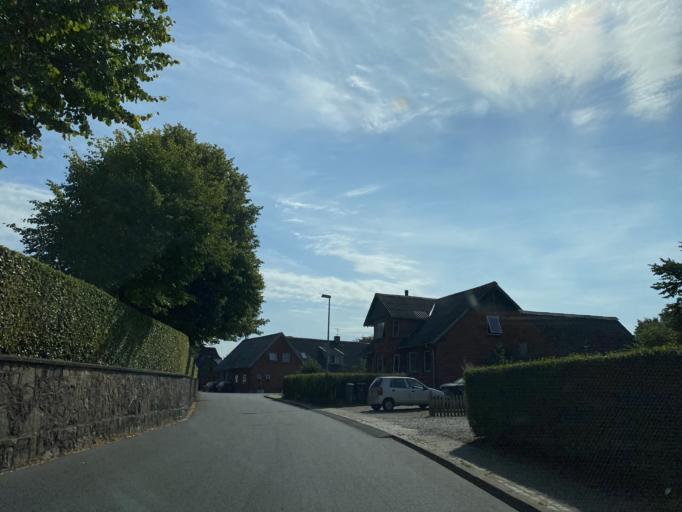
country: DK
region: Central Jutland
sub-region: Favrskov Kommune
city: Hammel
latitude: 56.2786
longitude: 9.8247
